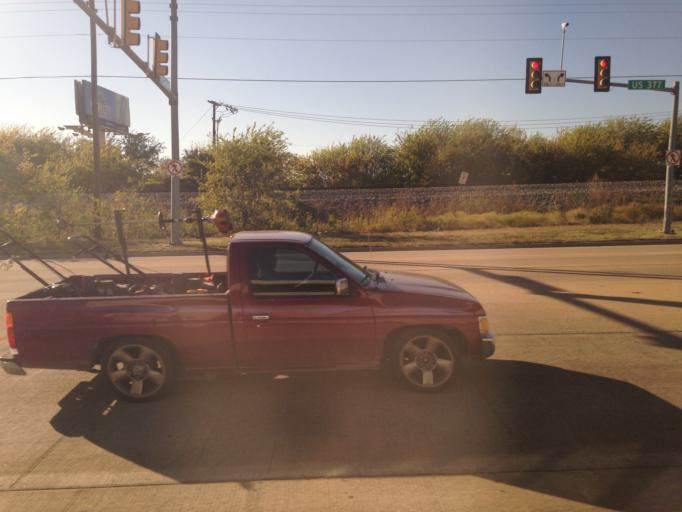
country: US
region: Texas
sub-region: Tarrant County
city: Watauga
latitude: 32.8863
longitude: -97.2599
